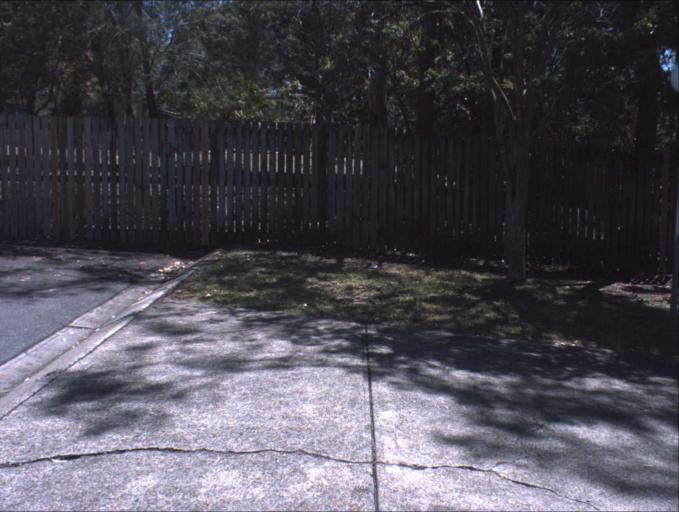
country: AU
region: Queensland
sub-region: Logan
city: Woodridge
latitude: -27.6295
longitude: 153.1045
